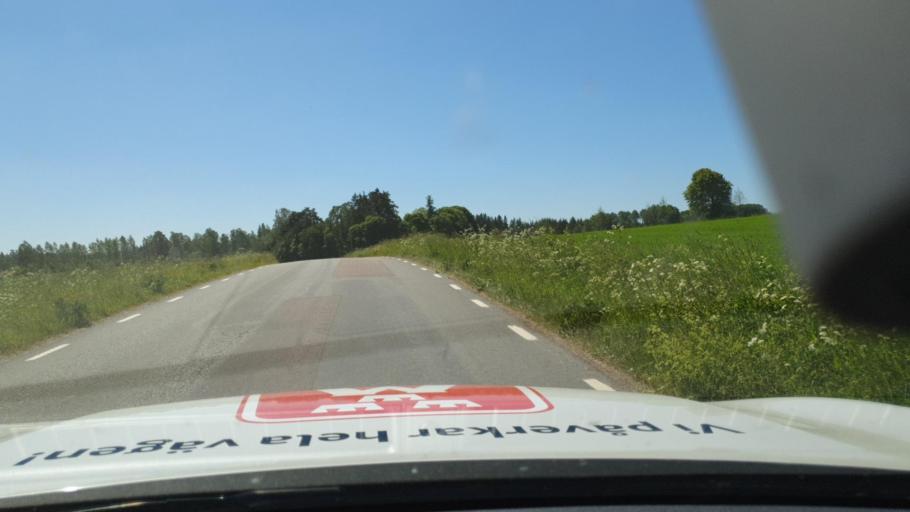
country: SE
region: Joenkoeping
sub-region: Habo Kommun
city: Habo
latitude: 57.8908
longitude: 14.0363
